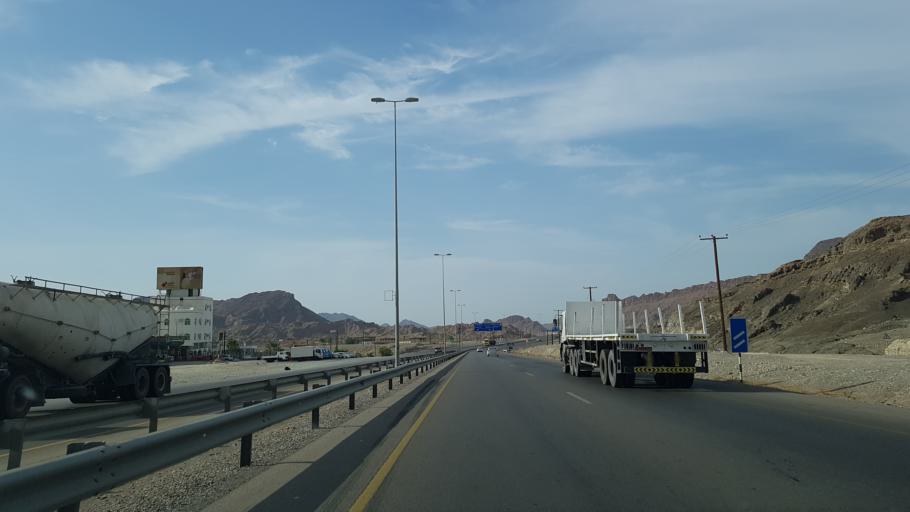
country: OM
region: Muhafazat ad Dakhiliyah
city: Bidbid
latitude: 23.4269
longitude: 58.1209
